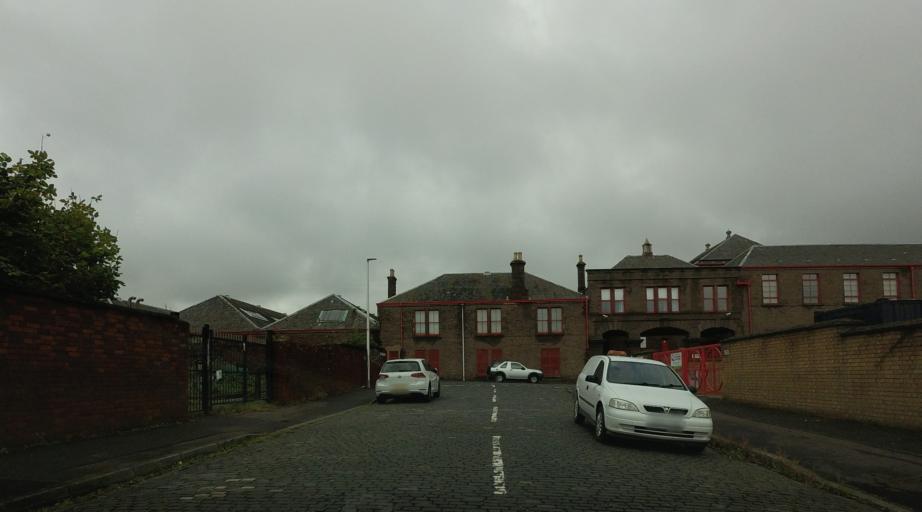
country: GB
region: Scotland
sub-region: Dundee City
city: Dundee
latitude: 56.4701
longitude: -2.9703
